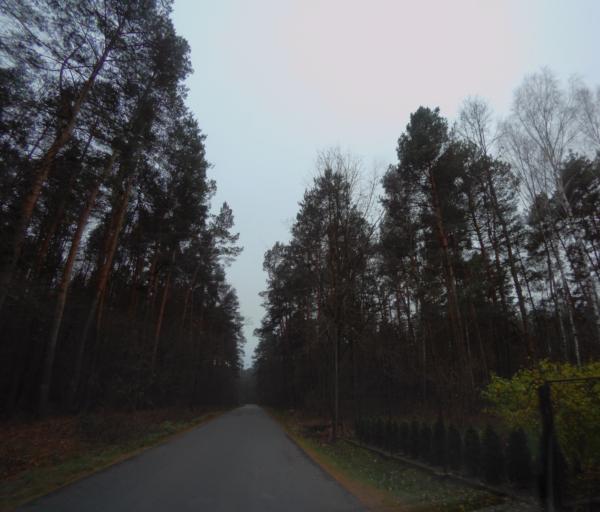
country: PL
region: Subcarpathian Voivodeship
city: Nowa Sarzyna
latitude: 50.3113
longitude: 22.3421
